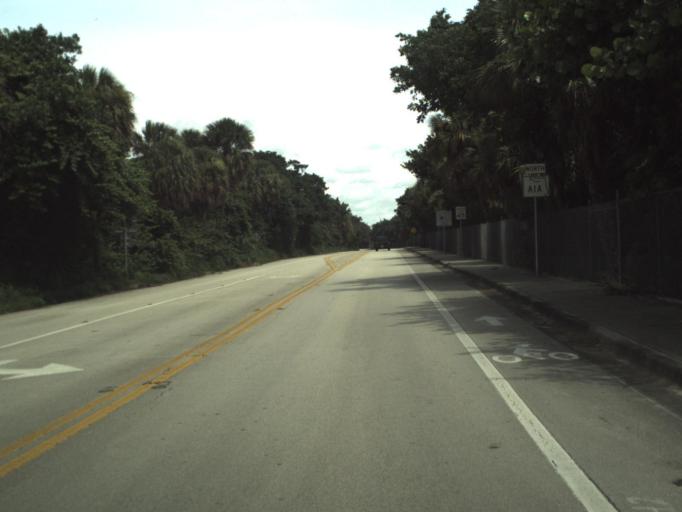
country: US
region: Florida
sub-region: Palm Beach County
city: Lake Park
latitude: 26.8245
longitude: -80.0445
